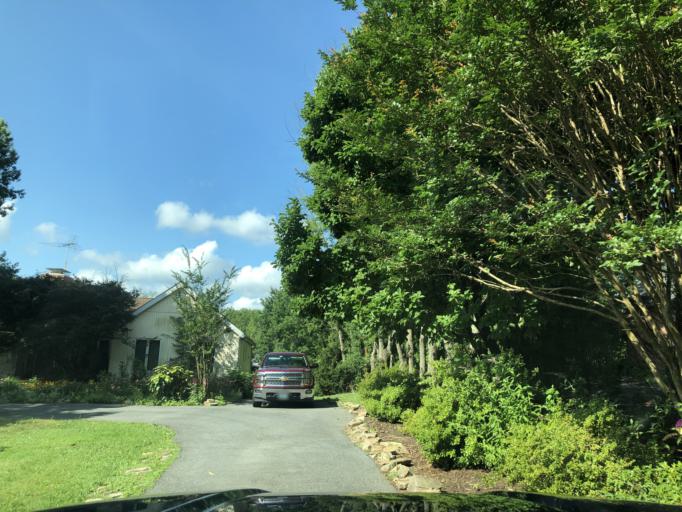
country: US
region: Maryland
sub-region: Howard County
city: Highland
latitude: 39.1895
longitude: -76.9377
